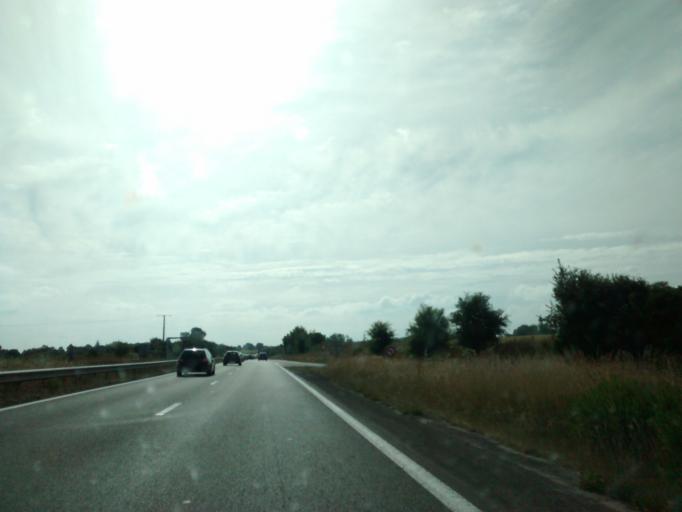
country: FR
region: Brittany
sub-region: Departement d'Ille-et-Vilaine
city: Saint-Gilles
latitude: 48.1599
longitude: -1.8370
